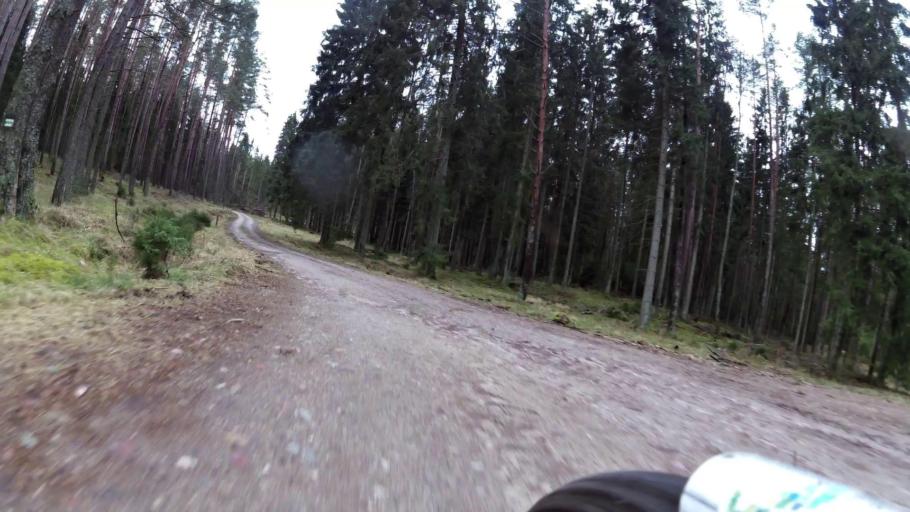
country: PL
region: Pomeranian Voivodeship
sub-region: Powiat bytowski
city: Borzytuchom
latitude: 54.2555
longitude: 17.3114
